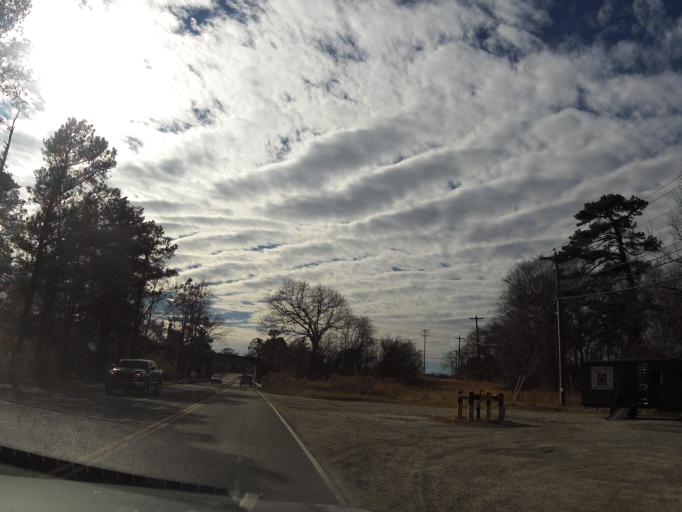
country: US
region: Virginia
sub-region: City of Franklin
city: Franklin
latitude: 36.6856
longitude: -76.9089
